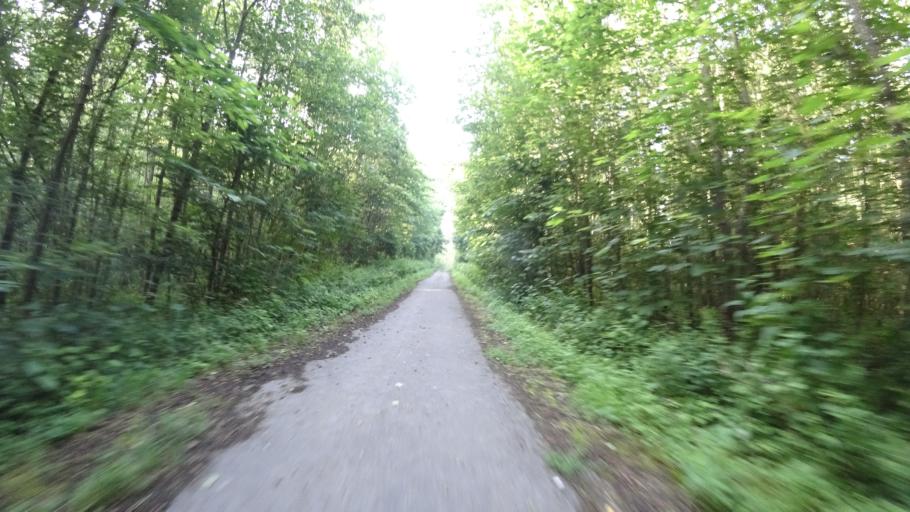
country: DE
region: North Rhine-Westphalia
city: Erwitte
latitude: 51.6365
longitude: 8.3778
